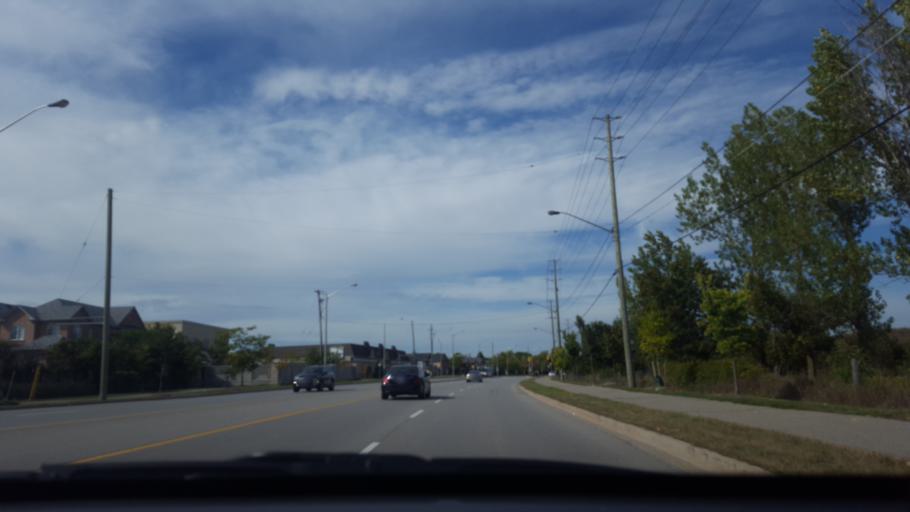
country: CA
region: Ontario
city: Vaughan
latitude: 43.8204
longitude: -79.6053
